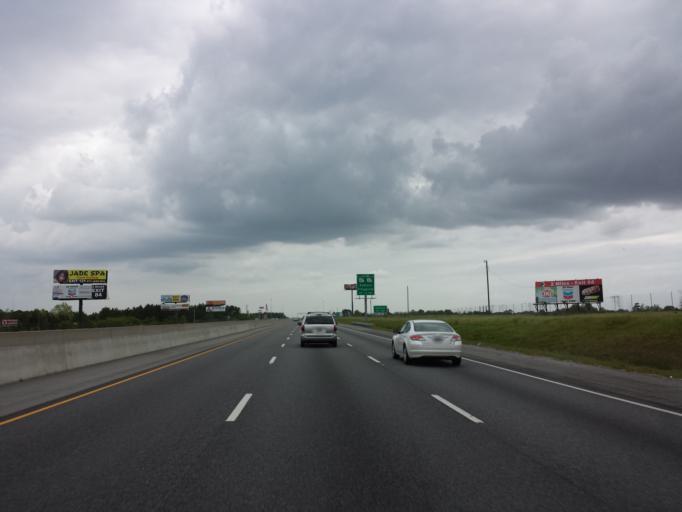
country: US
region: Georgia
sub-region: Turner County
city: Ashburn
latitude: 31.7005
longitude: -83.6320
